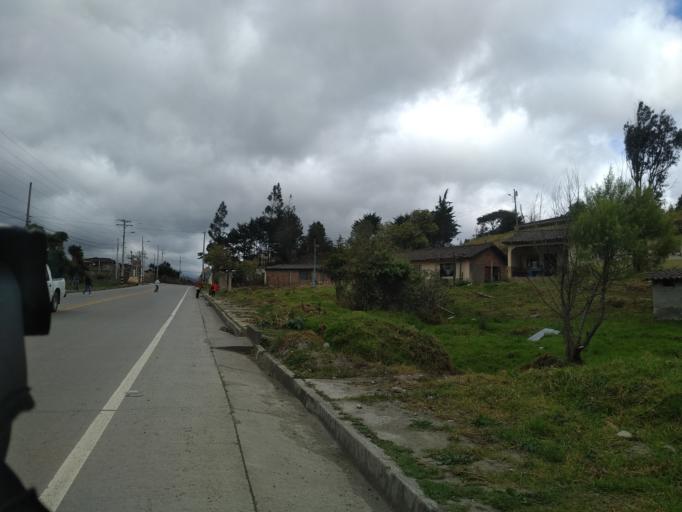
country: EC
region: Loja
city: Loja
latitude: -3.9534
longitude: -79.2493
